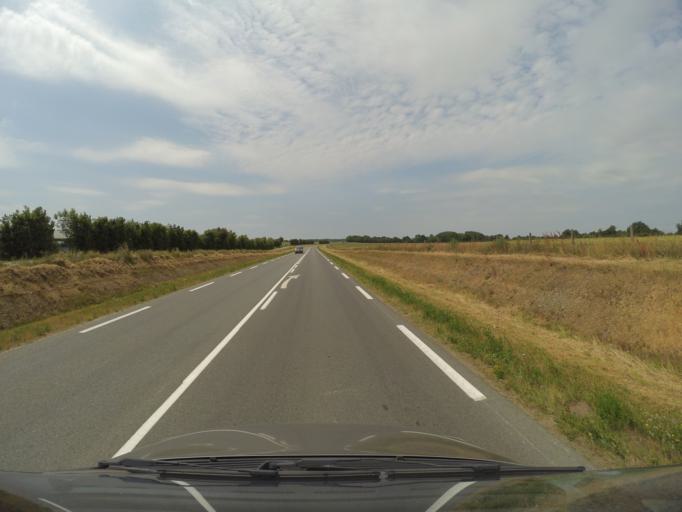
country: FR
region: Pays de la Loire
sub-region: Departement de la Vendee
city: Saint-Paul-en-Pareds
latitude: 46.8592
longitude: -0.9758
